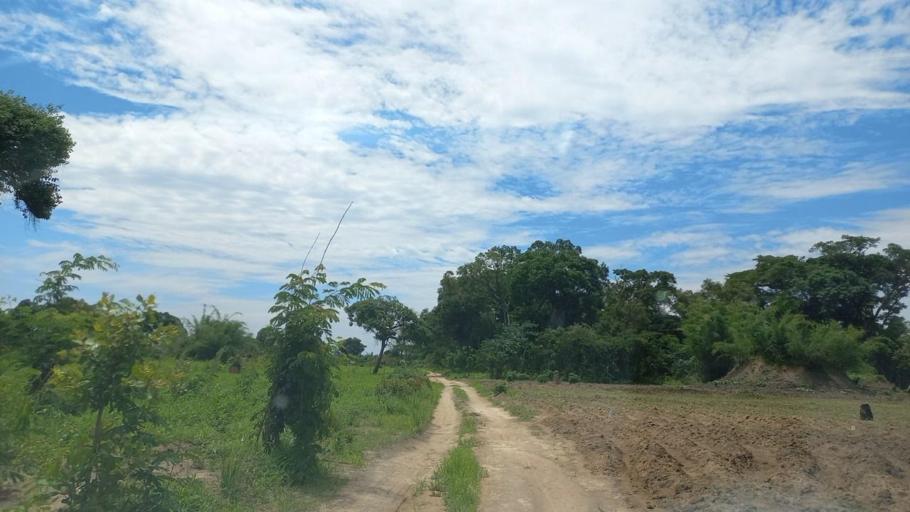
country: ZM
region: Copperbelt
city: Kitwe
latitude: -12.8002
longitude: 28.4015
